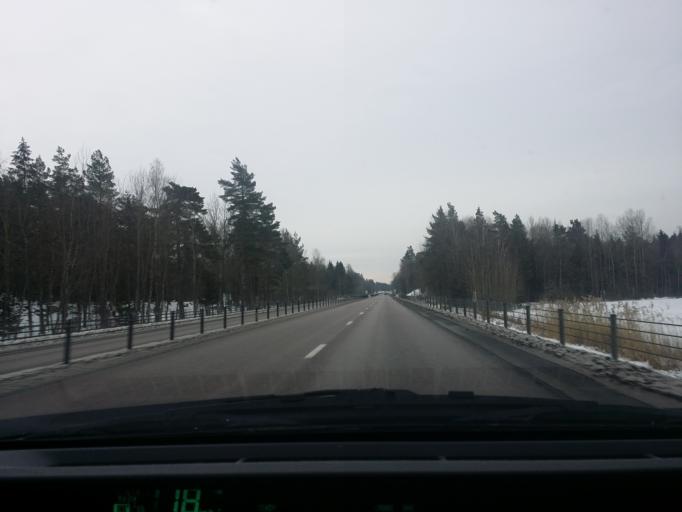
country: SE
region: Vaestra Goetaland
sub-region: Skovde Kommun
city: Stopen
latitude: 58.5235
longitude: 13.8244
